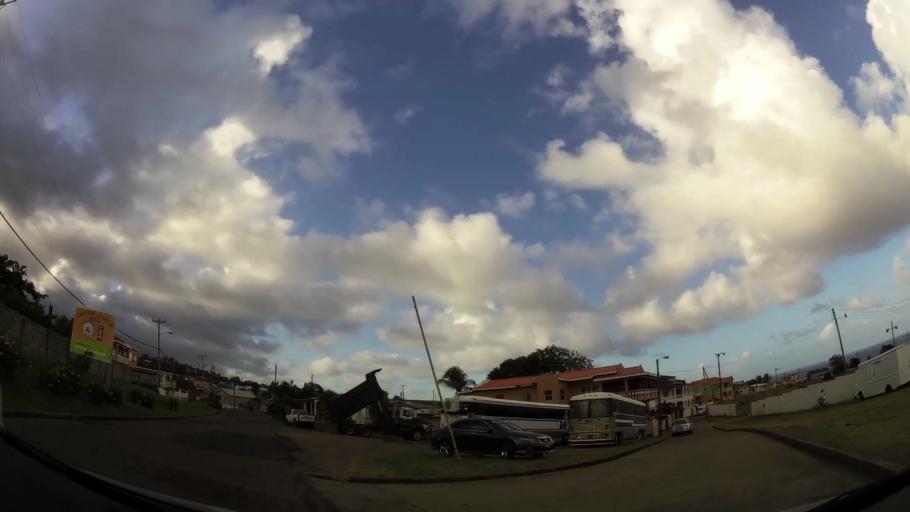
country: KN
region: Saint Mary Cayon
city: Cayon
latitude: 17.3487
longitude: -62.7284
